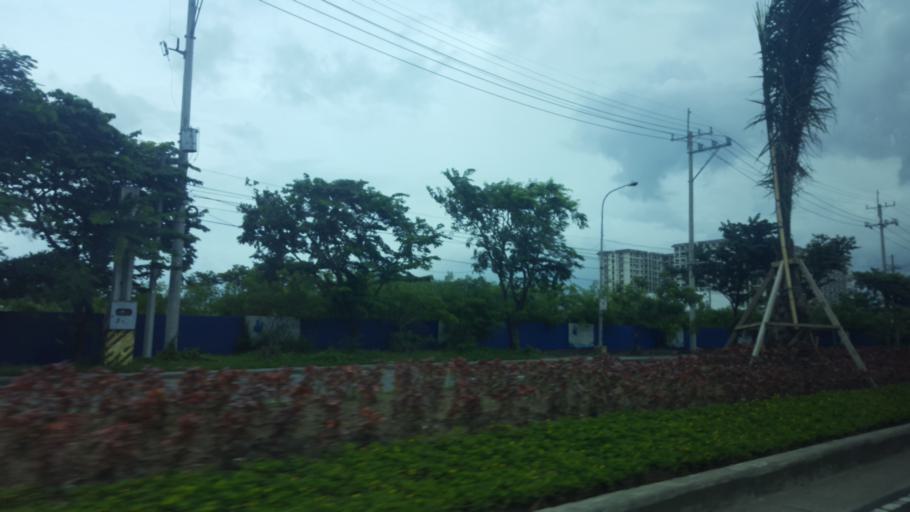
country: PH
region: Metro Manila
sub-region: Makati City
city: Makati City
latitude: 14.5268
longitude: 120.9902
